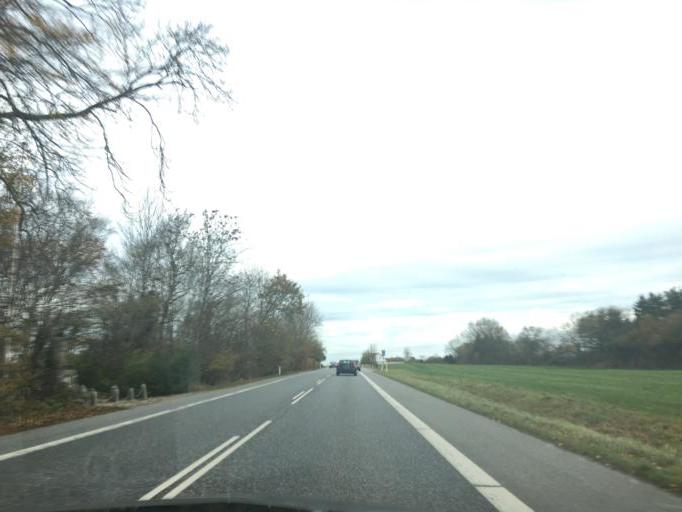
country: DK
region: South Denmark
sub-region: Vejle Kommune
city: Vejle
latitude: 55.6478
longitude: 9.5013
